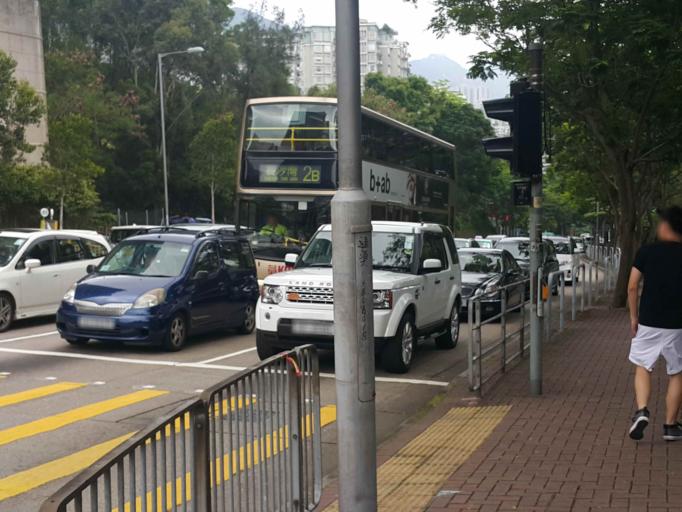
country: HK
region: Wong Tai Sin
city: Wong Tai Sin
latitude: 22.3395
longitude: 114.1721
